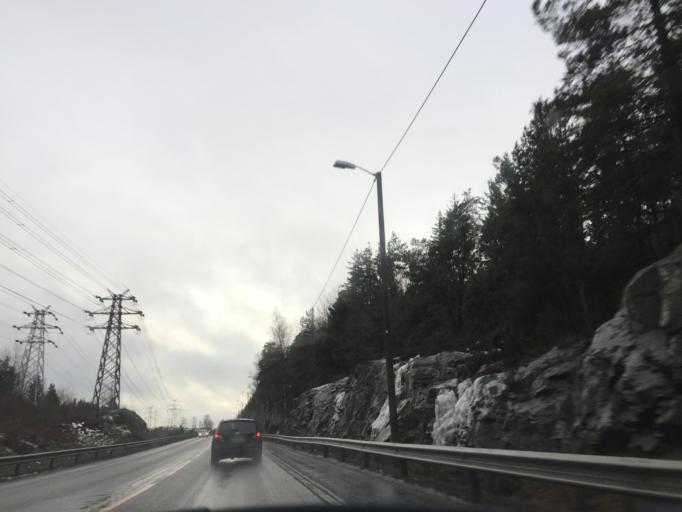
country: NO
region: Ostfold
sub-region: Moss
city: Moss
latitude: 59.4425
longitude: 10.6797
